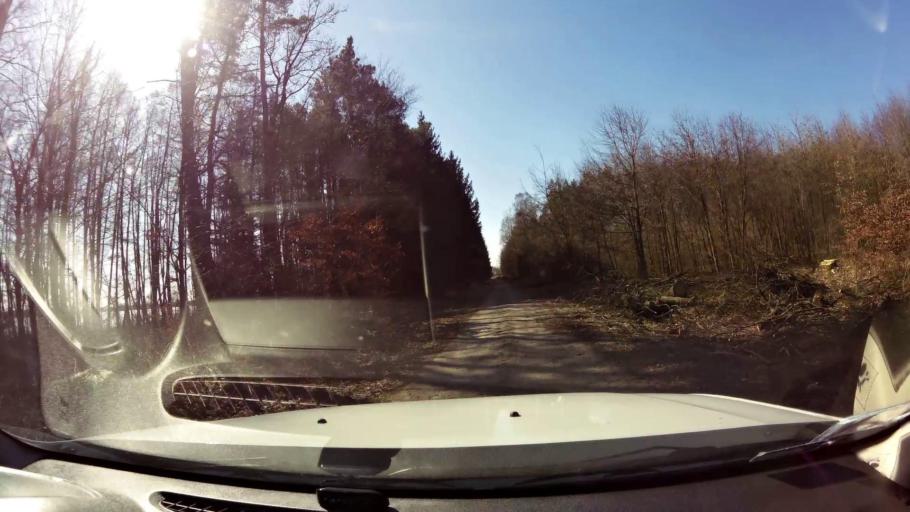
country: PL
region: West Pomeranian Voivodeship
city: Trzcinsko Zdroj
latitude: 53.0006
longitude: 14.6121
